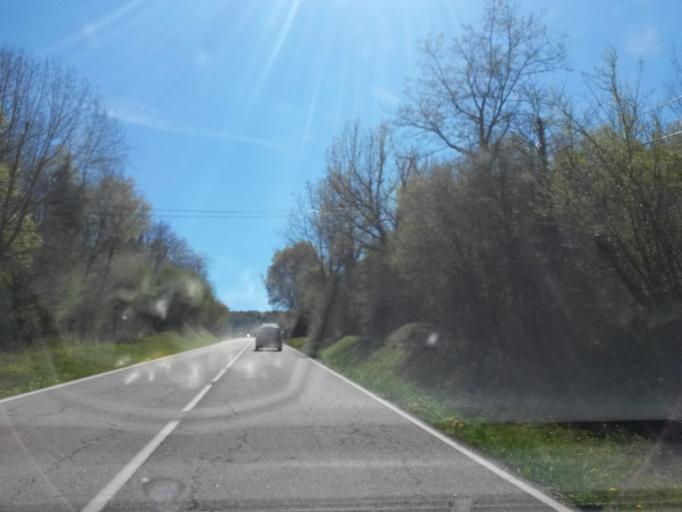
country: ES
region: Catalonia
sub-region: Provincia de Girona
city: Sant Cristofol de les Fonts
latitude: 42.1509
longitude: 2.5269
